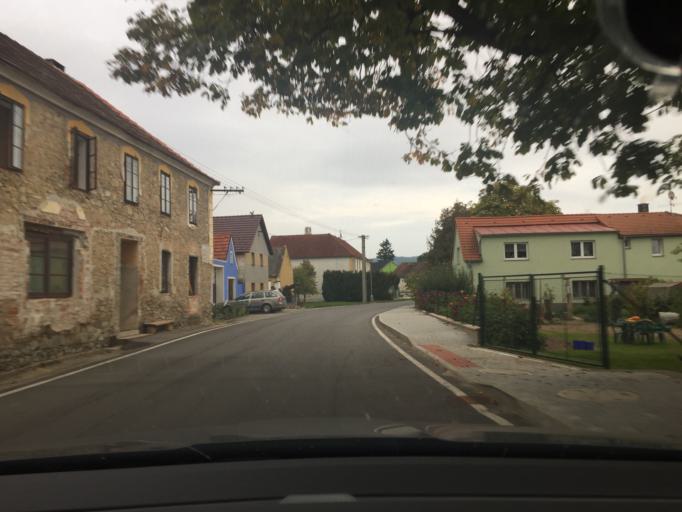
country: CZ
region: Jihocesky
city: Brloh
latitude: 48.9482
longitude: 14.2480
